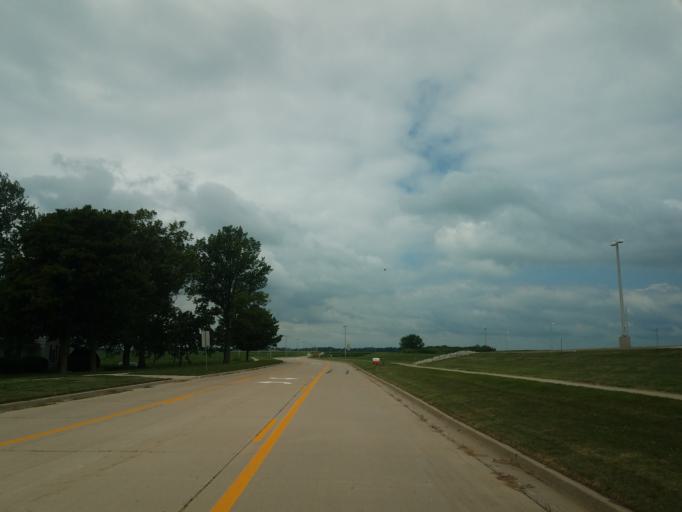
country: US
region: Illinois
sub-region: McLean County
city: Twin Grove
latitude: 40.4371
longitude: -89.0519
